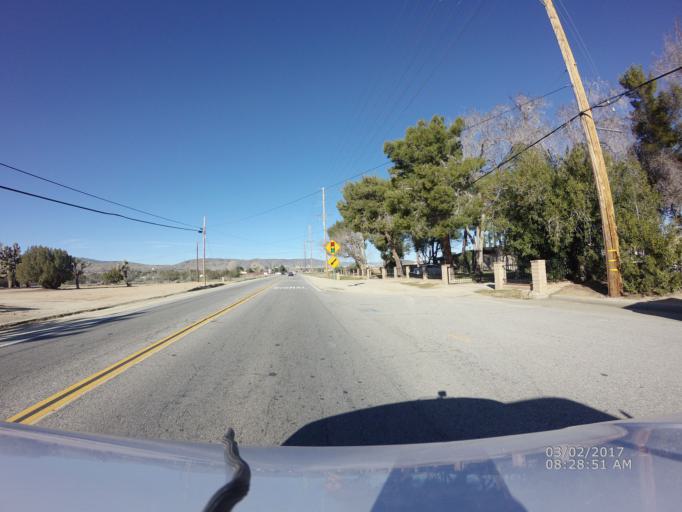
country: US
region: California
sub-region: Los Angeles County
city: Quartz Hill
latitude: 34.6311
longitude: -118.1811
